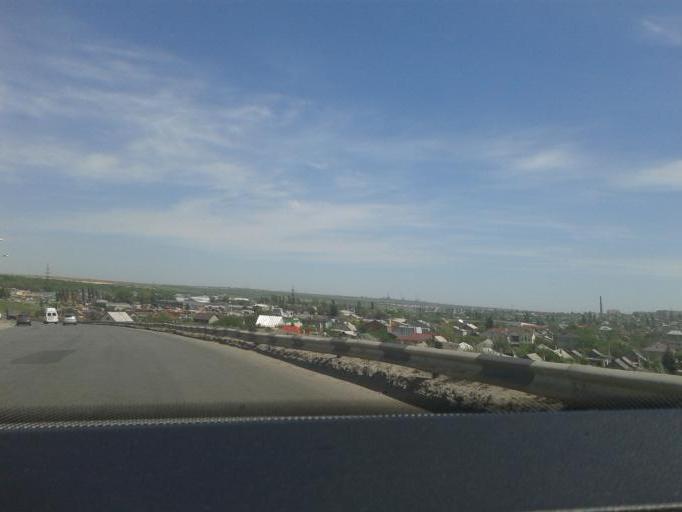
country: RU
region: Volgograd
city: Volgograd
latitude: 48.7690
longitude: 44.5190
